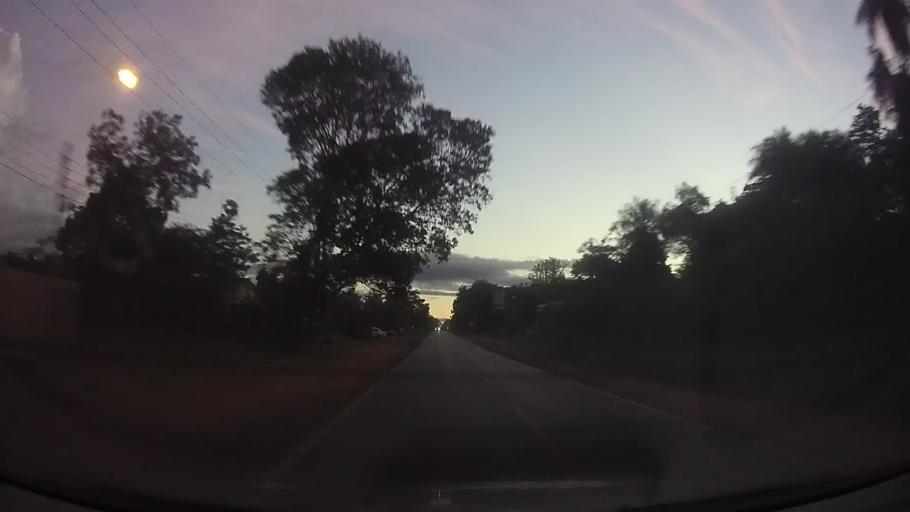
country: PY
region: Central
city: Itaugua
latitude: -25.4249
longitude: -57.3641
